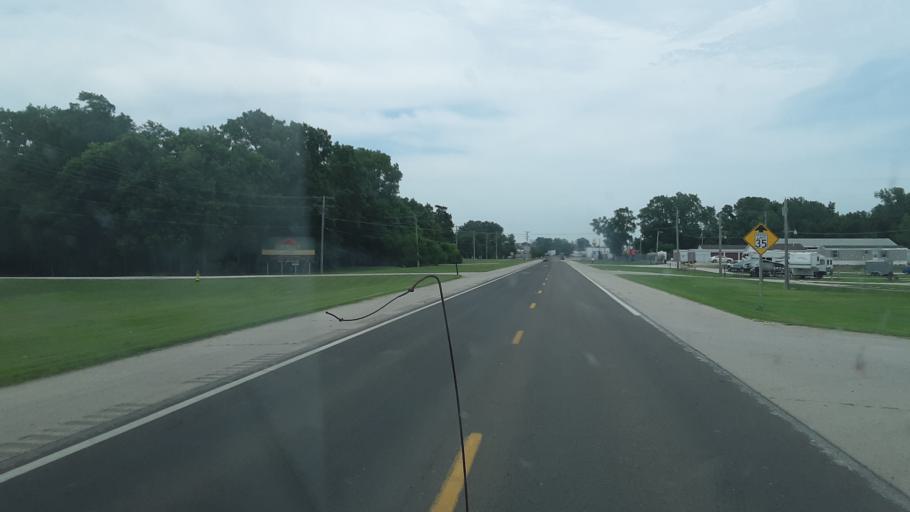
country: US
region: Kansas
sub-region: Allen County
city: Iola
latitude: 37.9220
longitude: -95.4176
